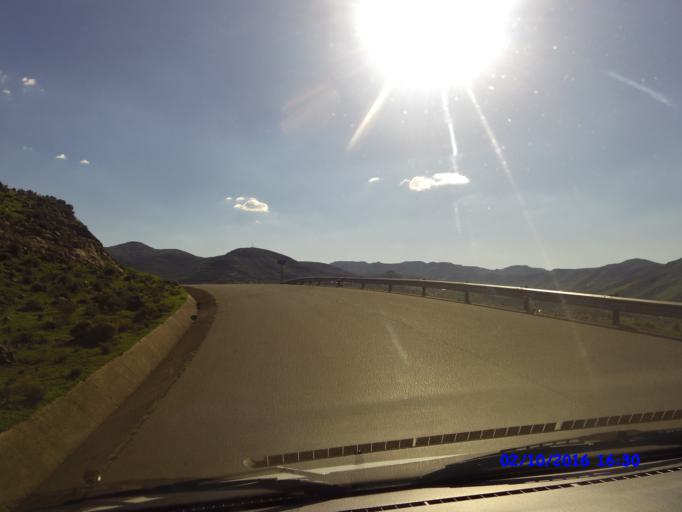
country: LS
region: Maseru
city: Nako
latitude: -29.4773
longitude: 28.0813
